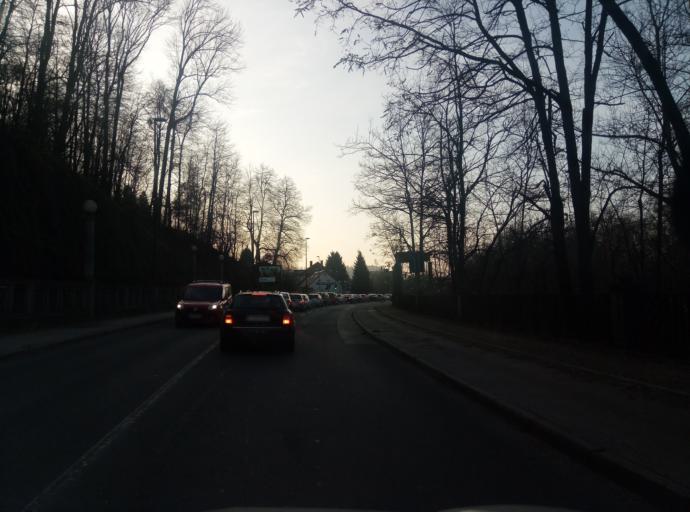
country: SI
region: Ljubljana
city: Ljubljana
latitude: 46.0481
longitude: 14.5337
